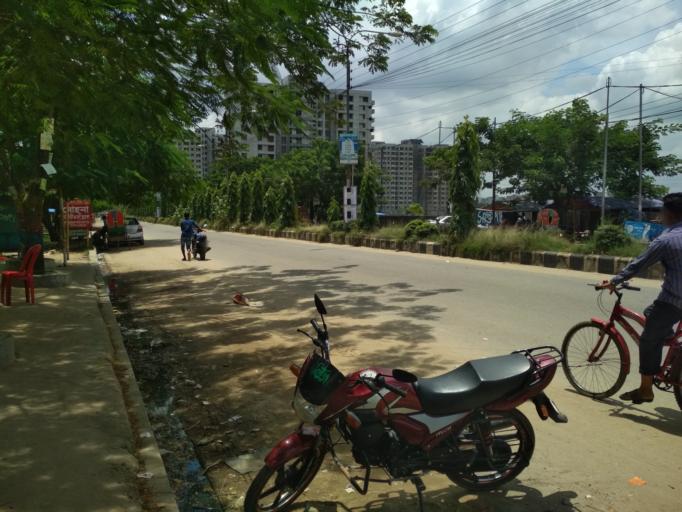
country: BD
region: Dhaka
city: Tungi
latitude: 23.8355
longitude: 90.3765
